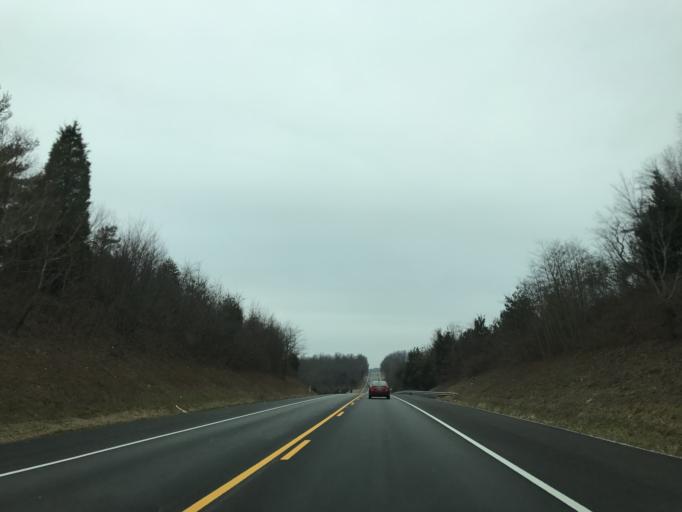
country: US
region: Maryland
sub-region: Carroll County
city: Westminster
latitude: 39.5984
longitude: -77.0442
